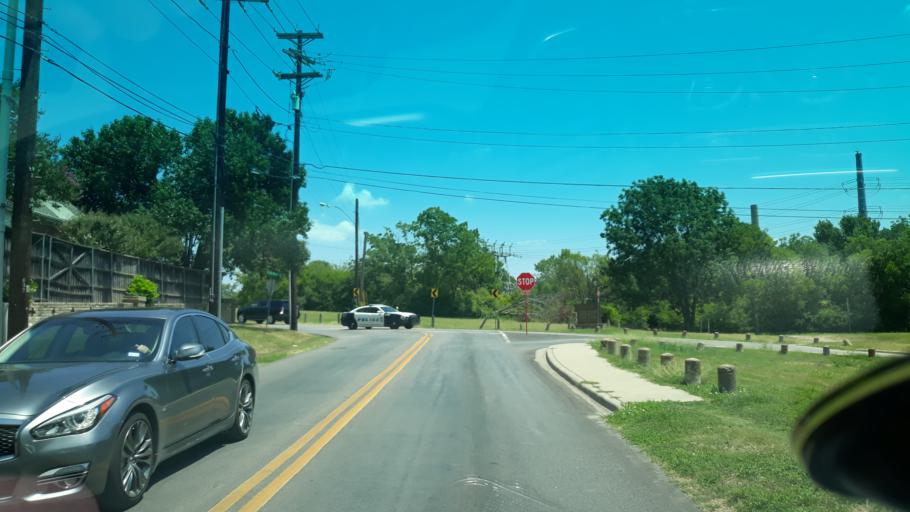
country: US
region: Texas
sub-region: Dallas County
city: Highland Park
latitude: 32.8201
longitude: -96.7315
